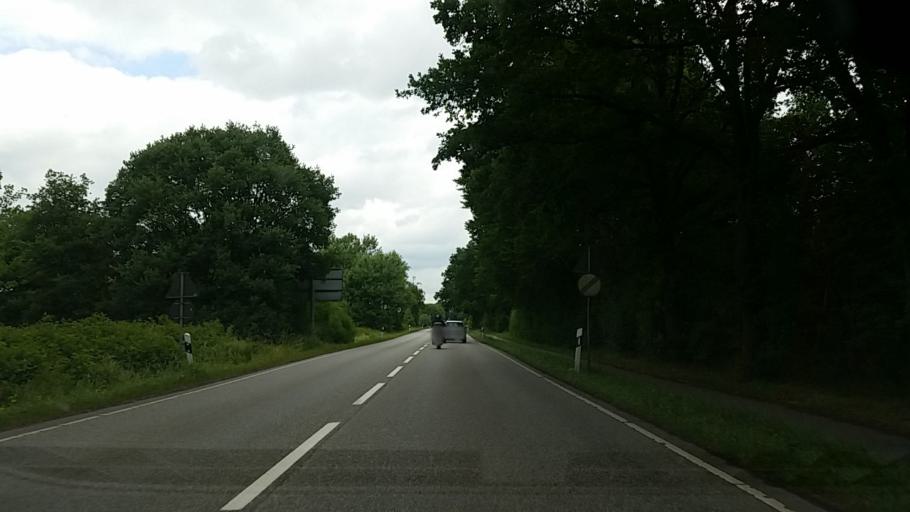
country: DE
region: Schleswig-Holstein
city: Tangstedt
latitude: 53.7152
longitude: 10.0793
